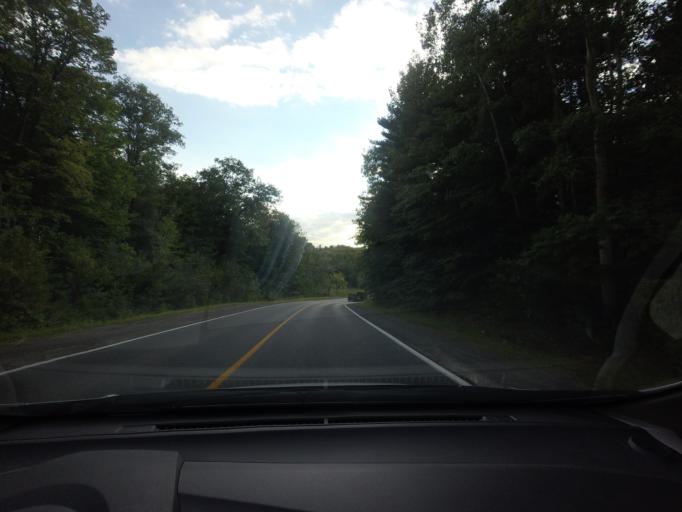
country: CA
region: Ontario
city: Perth
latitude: 44.6443
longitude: -76.5001
